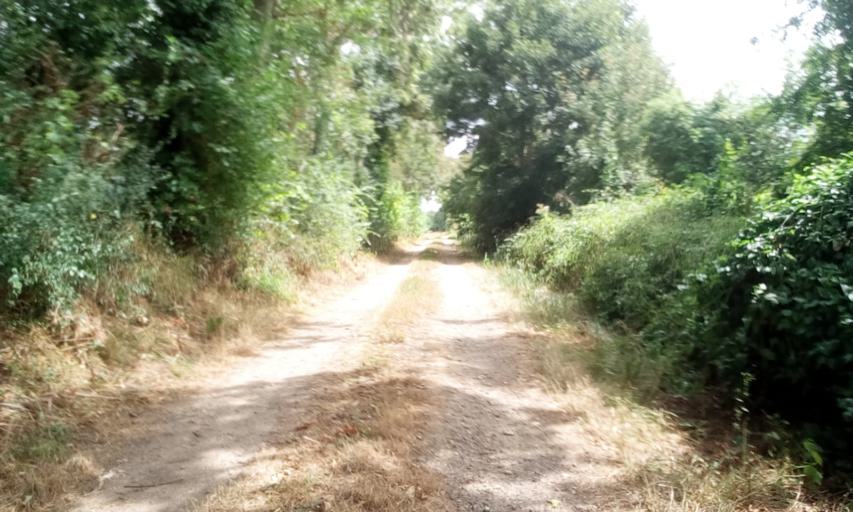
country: FR
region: Lower Normandy
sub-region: Departement du Calvados
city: Troarn
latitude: 49.1738
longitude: -0.2019
